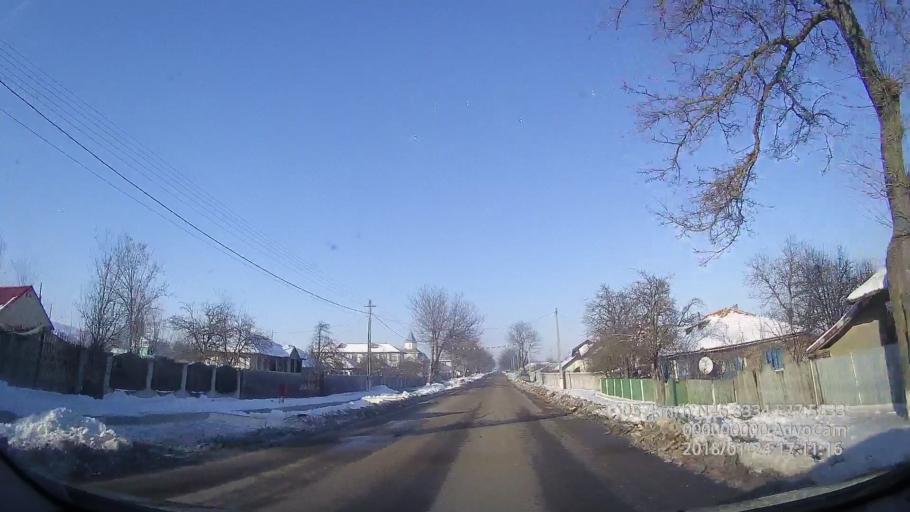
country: RO
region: Vaslui
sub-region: Comuna Vulturesti
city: Vulturesti
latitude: 46.8340
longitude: 27.5633
